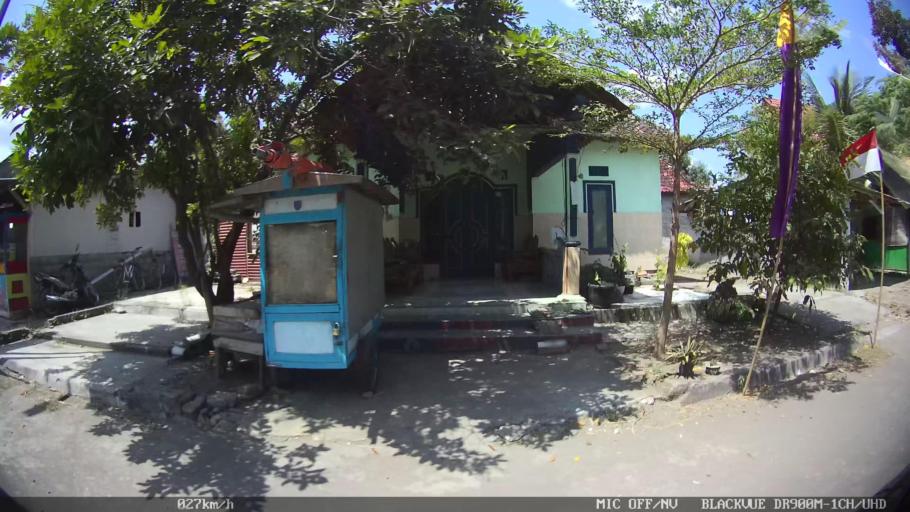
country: ID
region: Daerah Istimewa Yogyakarta
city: Pundong
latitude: -7.9383
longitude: 110.3741
